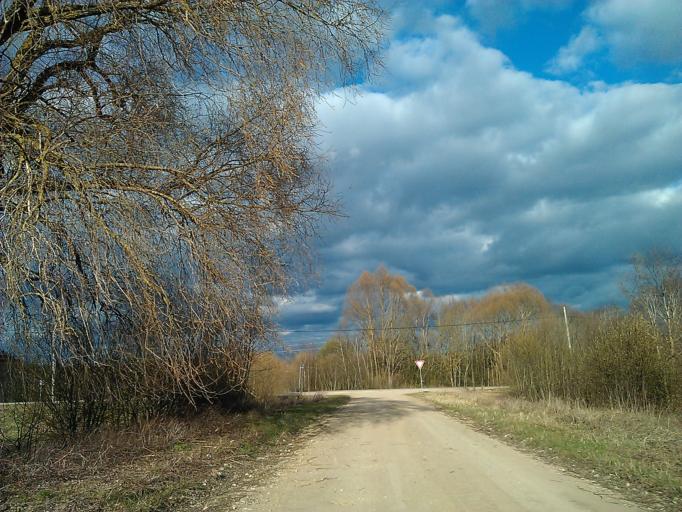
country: LV
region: Adazi
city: Adazi
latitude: 57.0658
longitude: 24.3606
